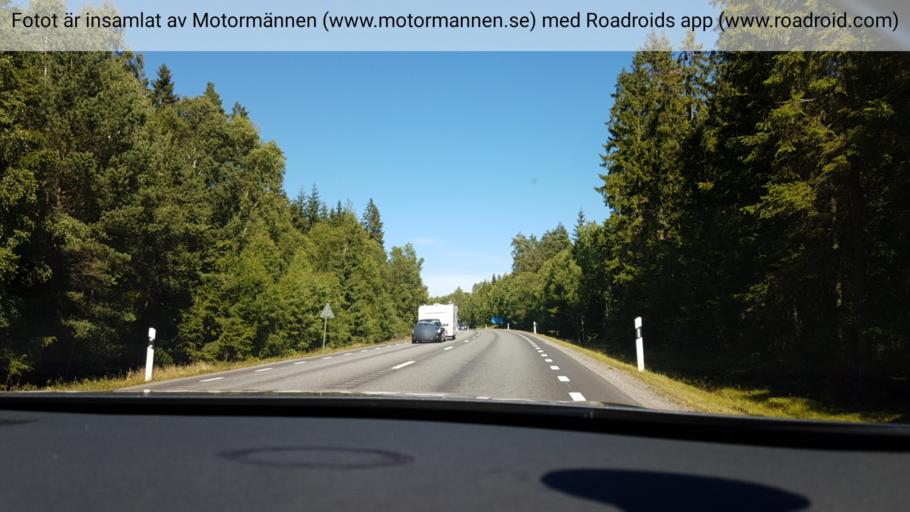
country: SE
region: Joenkoeping
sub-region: Varnamo Kommun
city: Varnamo
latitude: 57.1996
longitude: 14.0866
